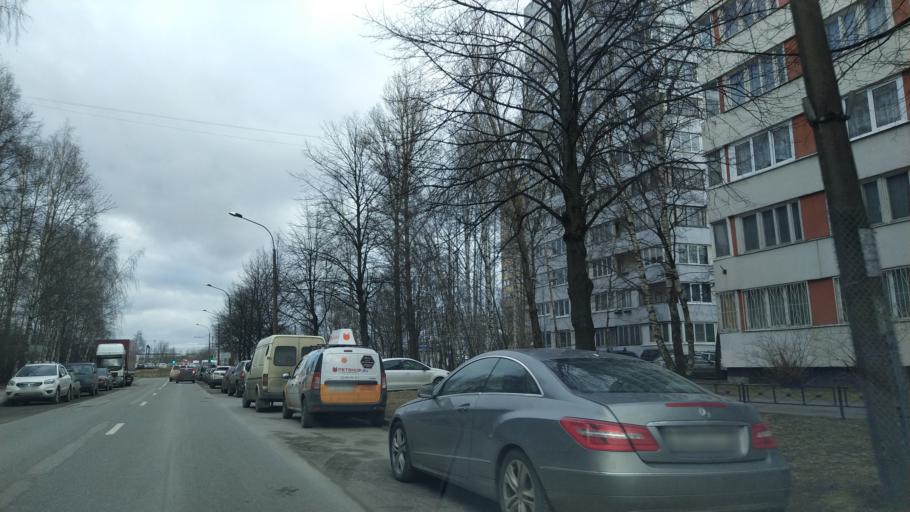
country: RU
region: Leningrad
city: Parnas
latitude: 60.0520
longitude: 30.3711
